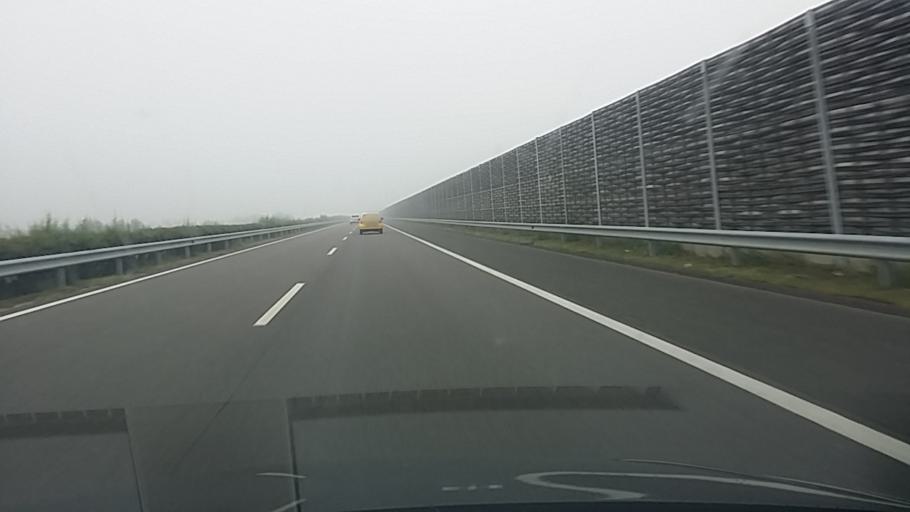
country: HU
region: Csongrad
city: Domaszek
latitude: 46.2720
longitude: 20.0399
